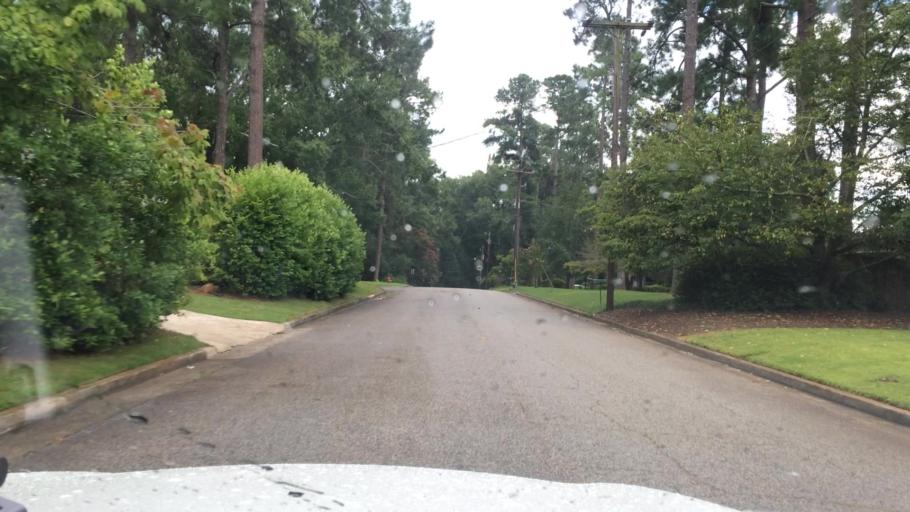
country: US
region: South Carolina
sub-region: Aiken County
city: North Augusta
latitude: 33.5051
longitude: -81.9877
